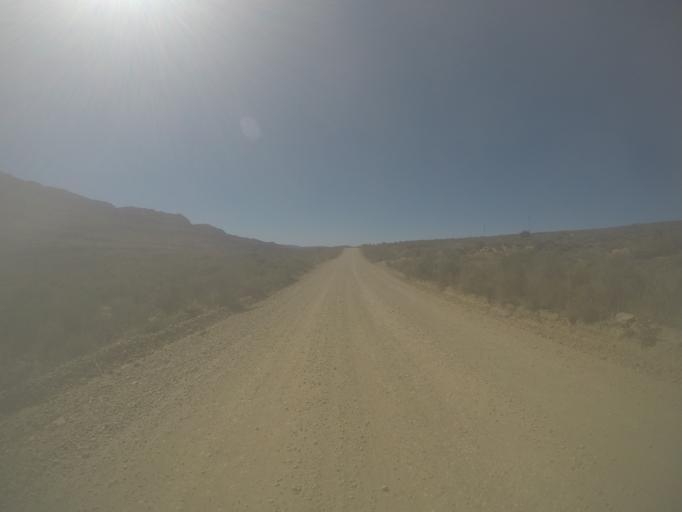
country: ZA
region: Western Cape
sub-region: West Coast District Municipality
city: Clanwilliam
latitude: -32.4954
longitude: 19.2692
